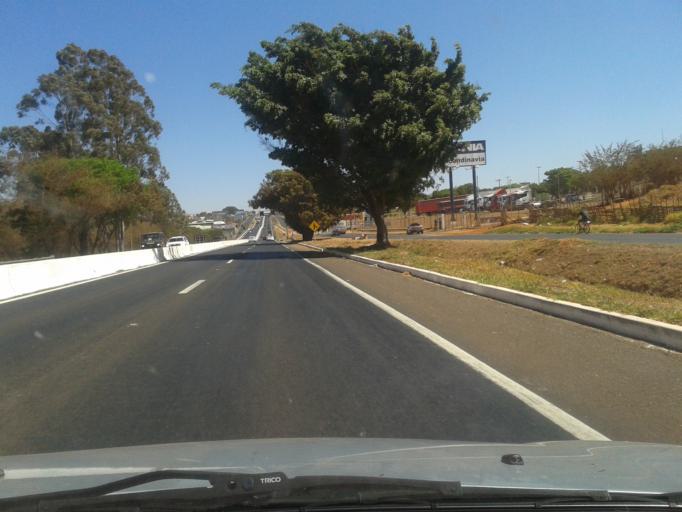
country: BR
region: Minas Gerais
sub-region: Uberlandia
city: Uberlandia
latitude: -18.9053
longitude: -48.2314
